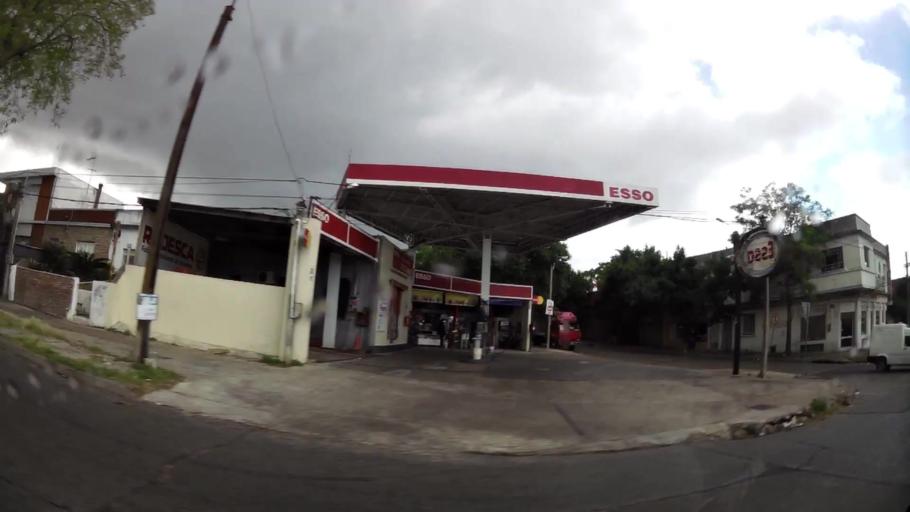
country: UY
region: Montevideo
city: Montevideo
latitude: -34.8540
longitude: -56.1727
